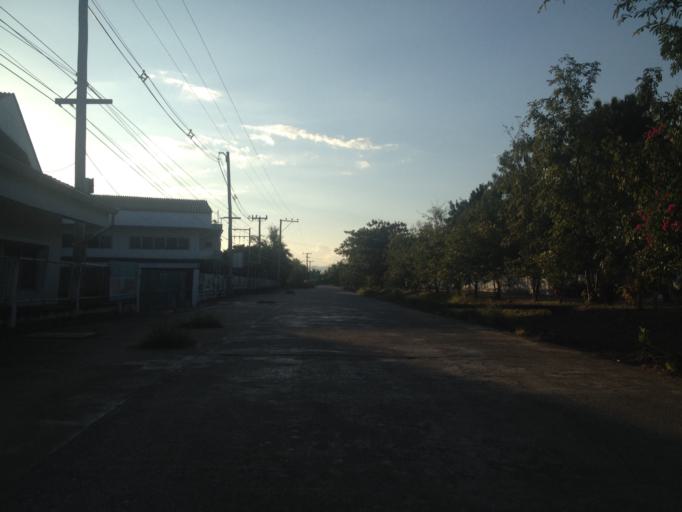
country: TH
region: Chiang Mai
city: San Pa Tong
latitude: 18.6493
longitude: 98.8896
